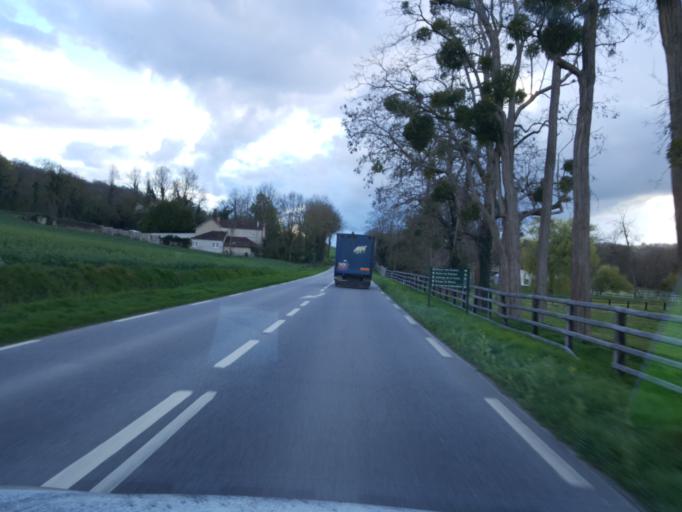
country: FR
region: Ile-de-France
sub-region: Departement des Yvelines
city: Septeuil
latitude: 48.9198
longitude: 1.6919
